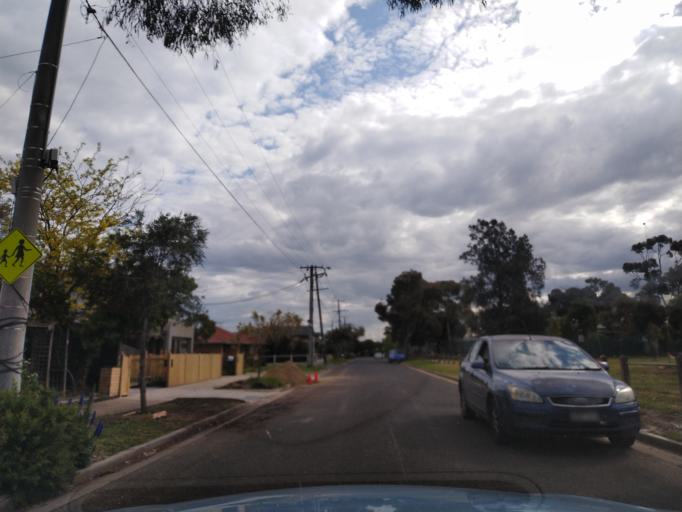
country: AU
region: Victoria
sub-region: Hobsons Bay
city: Altona North
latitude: -37.8426
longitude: 144.8510
